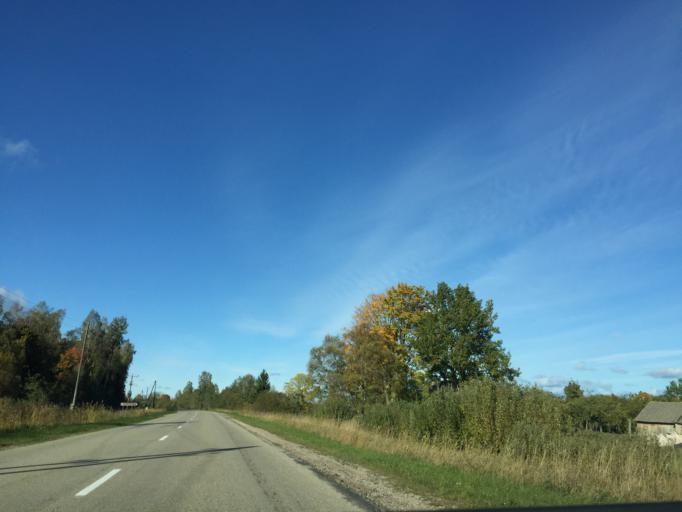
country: LV
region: Rojas
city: Roja
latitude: 57.4433
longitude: 22.9029
